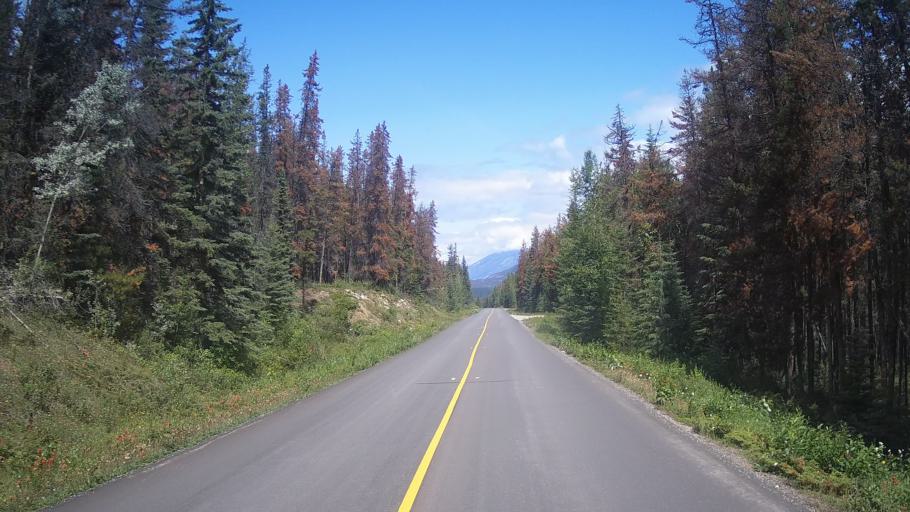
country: CA
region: Alberta
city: Jasper Park Lodge
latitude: 52.7790
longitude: -118.0325
